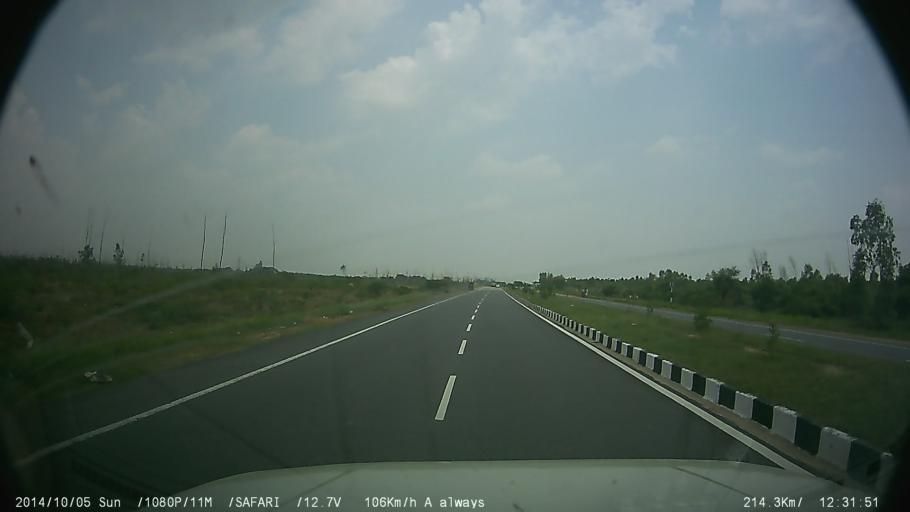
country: IN
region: Tamil Nadu
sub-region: Cuddalore
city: Vriddhachalam
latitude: 11.7131
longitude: 79.2059
